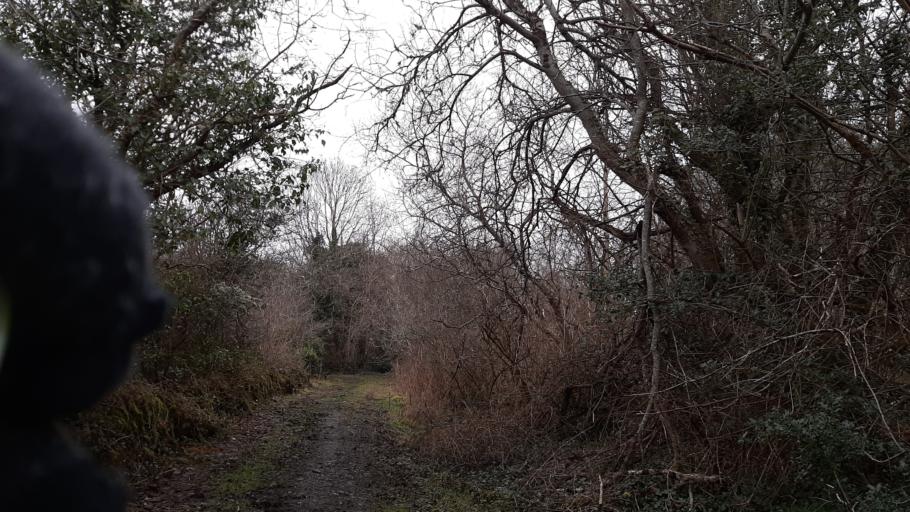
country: IE
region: Connaught
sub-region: County Galway
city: Gaillimh
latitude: 53.2938
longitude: -9.0631
